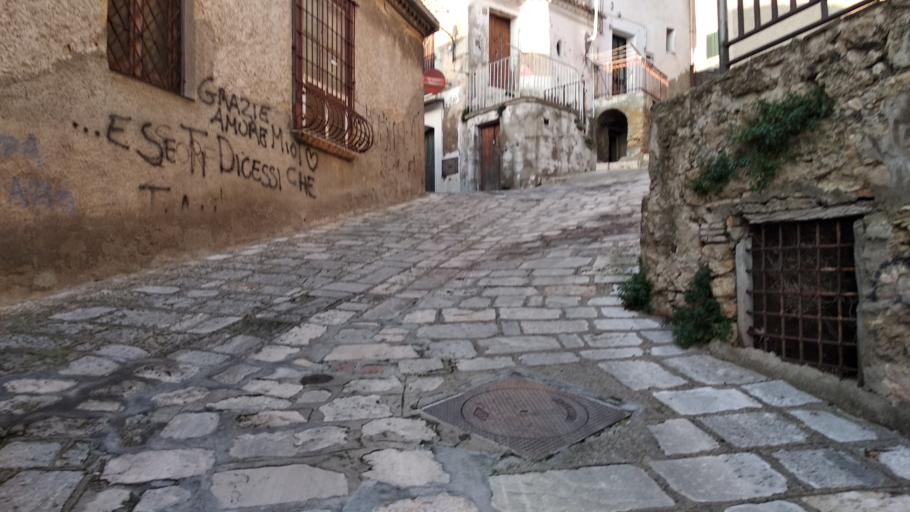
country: IT
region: Basilicate
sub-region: Provincia di Matera
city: Tricarico
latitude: 40.6209
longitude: 16.1464
